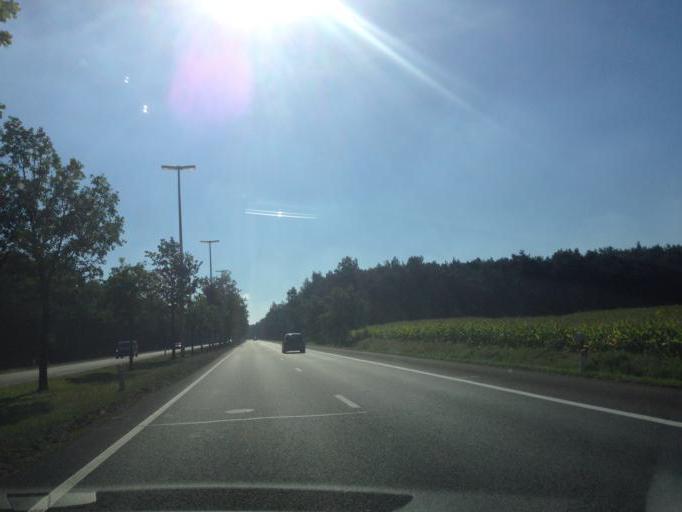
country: BE
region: Flanders
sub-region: Provincie Limburg
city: Lommel
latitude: 51.2195
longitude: 5.3360
